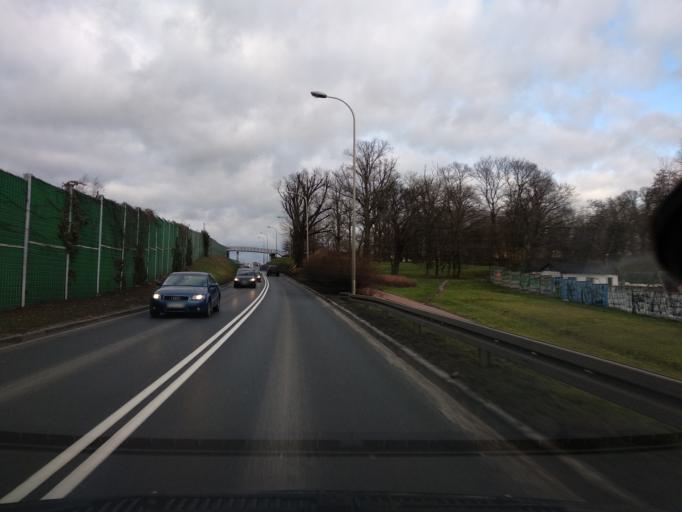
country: PL
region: Greater Poland Voivodeship
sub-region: Kalisz
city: Kalisz
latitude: 51.7744
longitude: 18.0760
